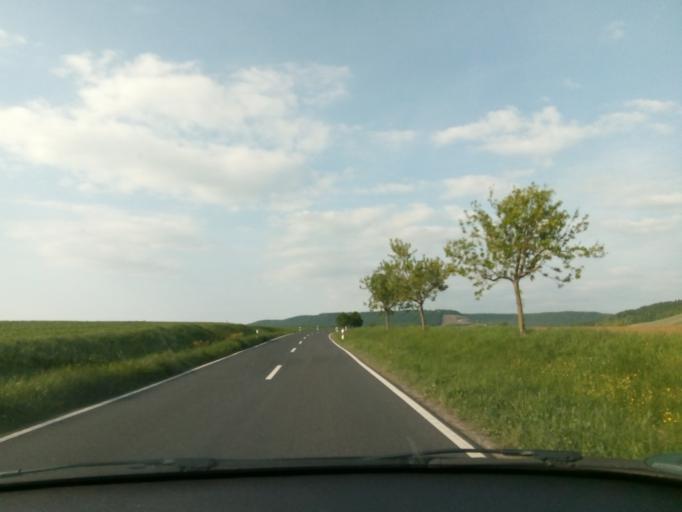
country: DE
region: Bavaria
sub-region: Regierungsbezirk Unterfranken
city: Oberschwarzach
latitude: 49.8534
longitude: 10.4077
